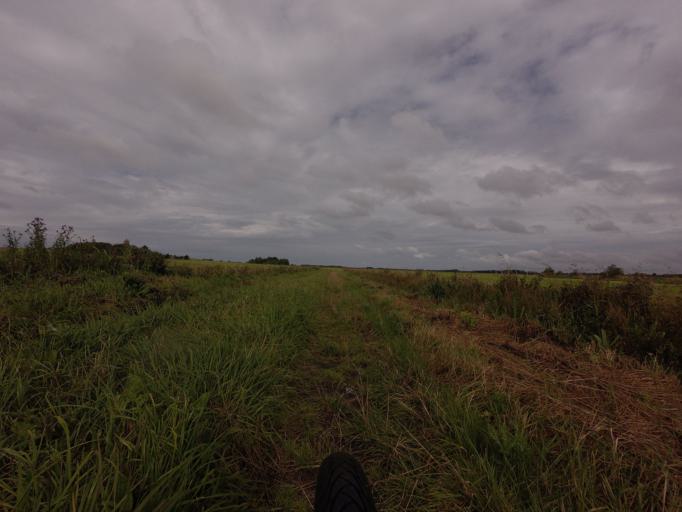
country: DK
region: North Denmark
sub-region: Jammerbugt Kommune
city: Pandrup
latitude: 57.3154
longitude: 9.7433
